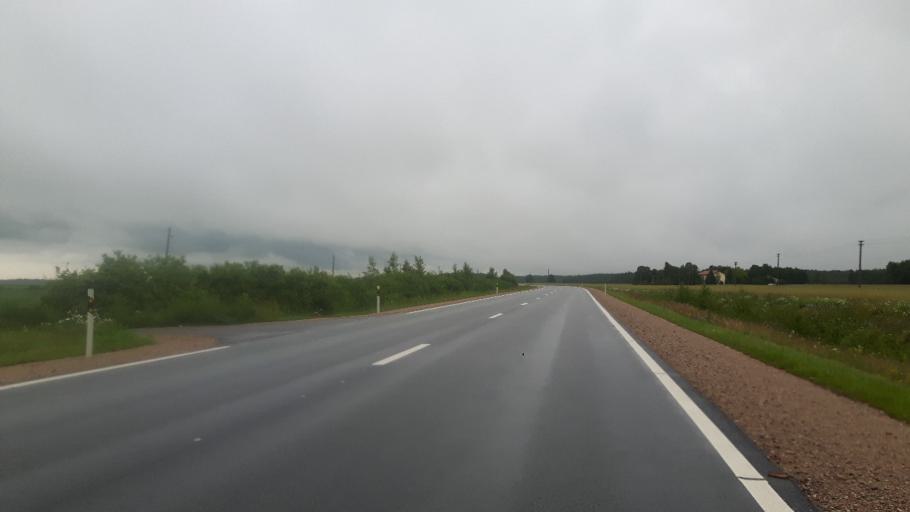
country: LV
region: Nica
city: Nica
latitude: 56.2940
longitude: 21.0961
